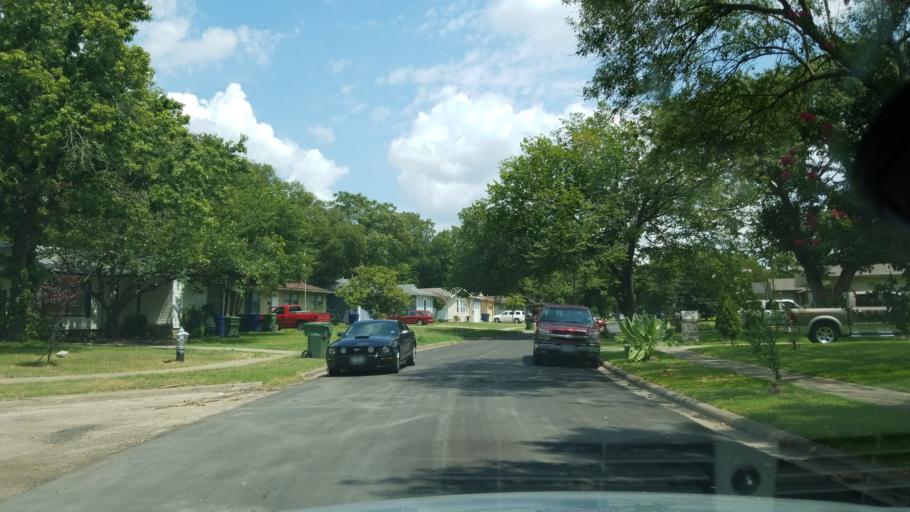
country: US
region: Texas
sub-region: Dallas County
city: Garland
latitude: 32.9217
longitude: -96.6549
